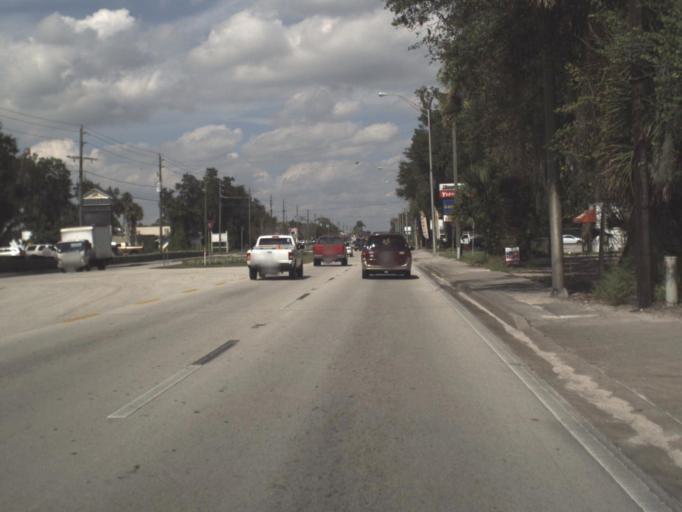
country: US
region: Florida
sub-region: Okeechobee County
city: Okeechobee
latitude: 27.2253
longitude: -80.8298
